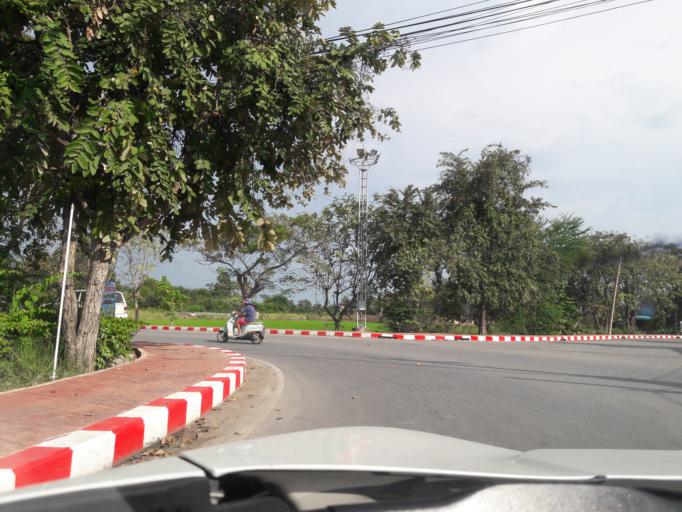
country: TH
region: Lop Buri
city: Ban Mi
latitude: 15.0364
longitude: 100.5423
